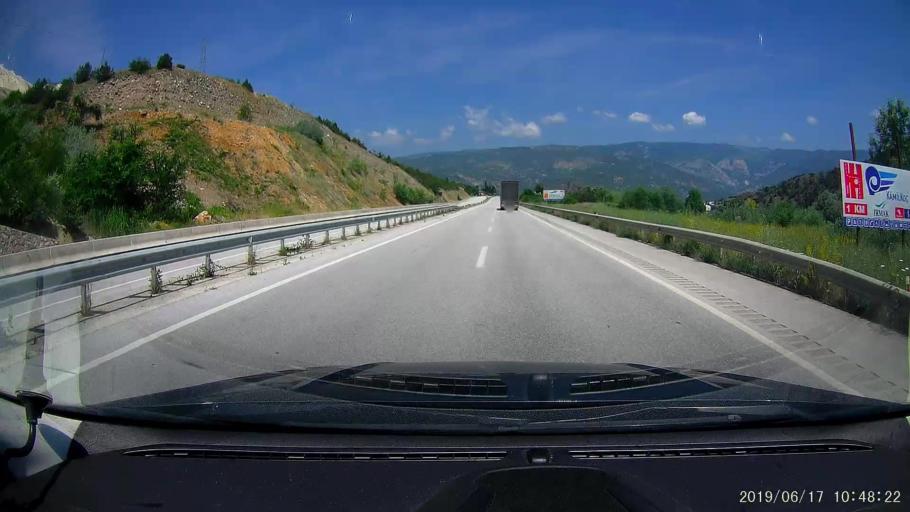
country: TR
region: Corum
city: Hacihamza
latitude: 41.0875
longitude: 34.4281
